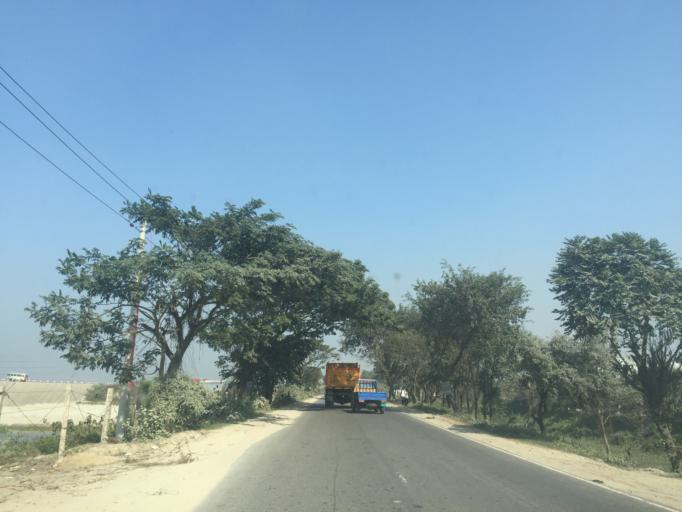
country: BD
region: Dhaka
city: Tungi
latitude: 23.8493
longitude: 90.3404
